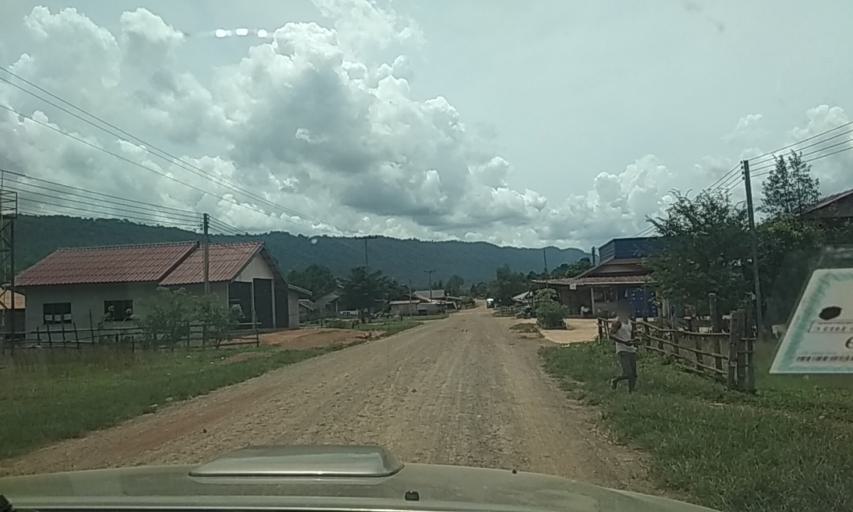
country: LA
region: Bolikhamxai
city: Ban Nahin
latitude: 18.1402
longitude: 104.7605
